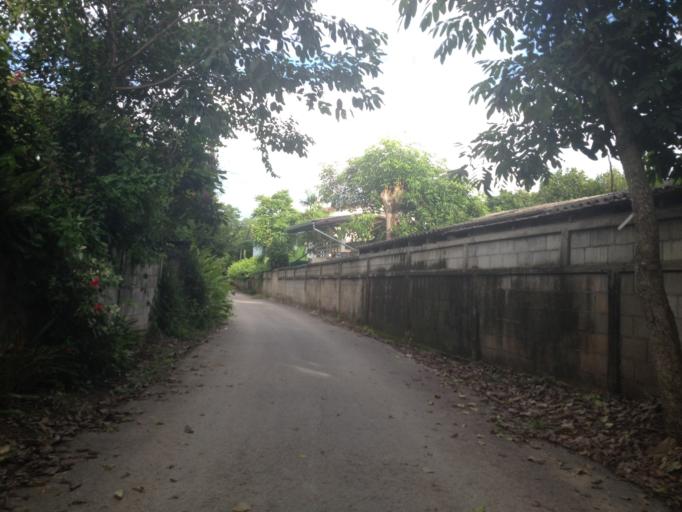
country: TH
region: Chiang Mai
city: Hang Dong
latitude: 18.6879
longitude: 98.8933
